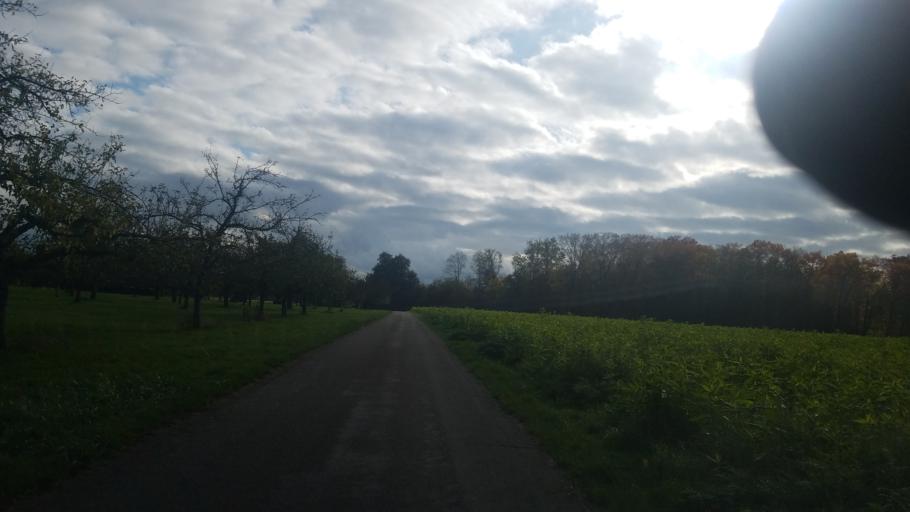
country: DE
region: Baden-Wuerttemberg
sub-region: Freiburg Region
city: Rheinau
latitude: 48.6784
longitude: 7.9803
